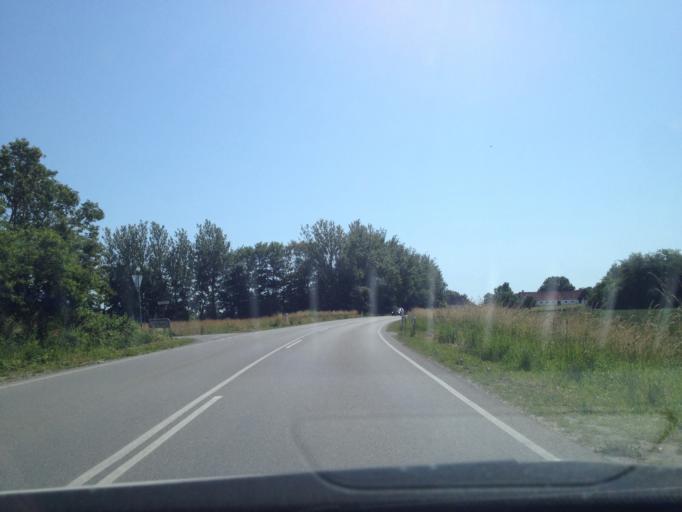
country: DK
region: Central Jutland
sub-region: Samso Kommune
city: Tranebjerg
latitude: 55.8542
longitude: 10.5731
